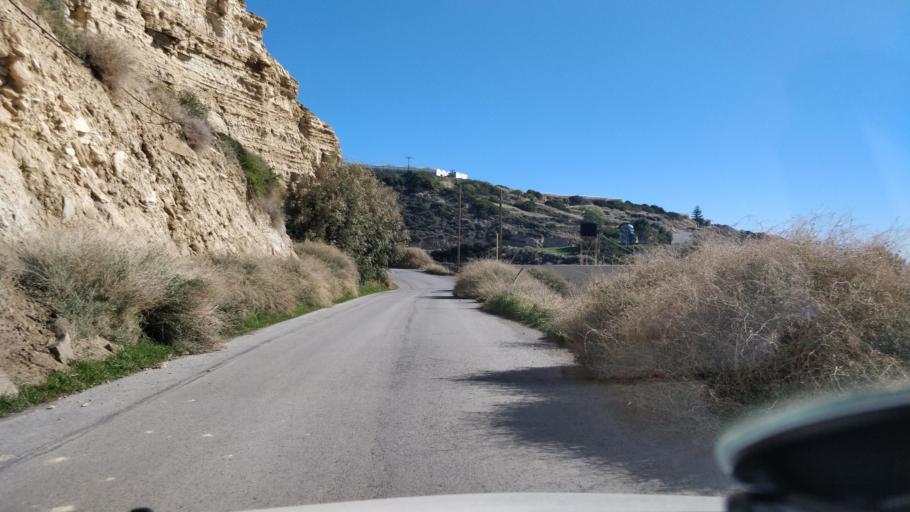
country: GR
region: Crete
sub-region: Nomos Lasithiou
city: Gra Liyia
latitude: 34.9871
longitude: 25.4805
